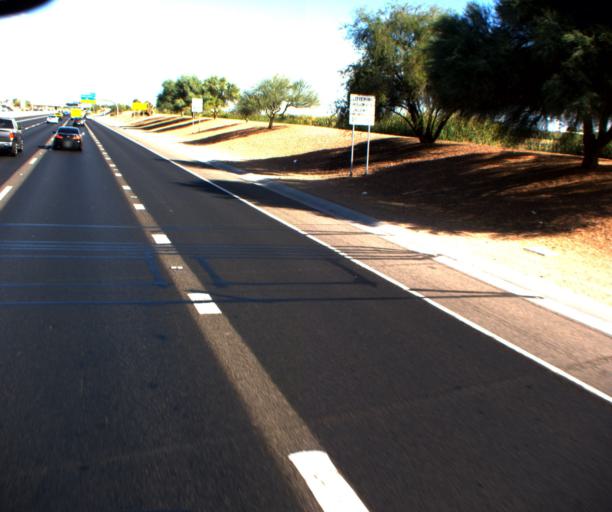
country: US
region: Arizona
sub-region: Maricopa County
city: Tolleson
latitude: 33.4864
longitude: -112.2637
